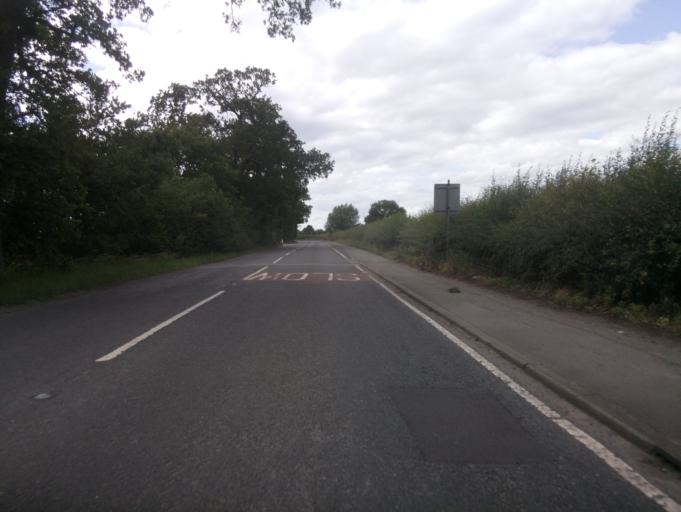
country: GB
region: England
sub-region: Warwickshire
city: Nuneaton
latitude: 52.5444
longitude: -1.4705
